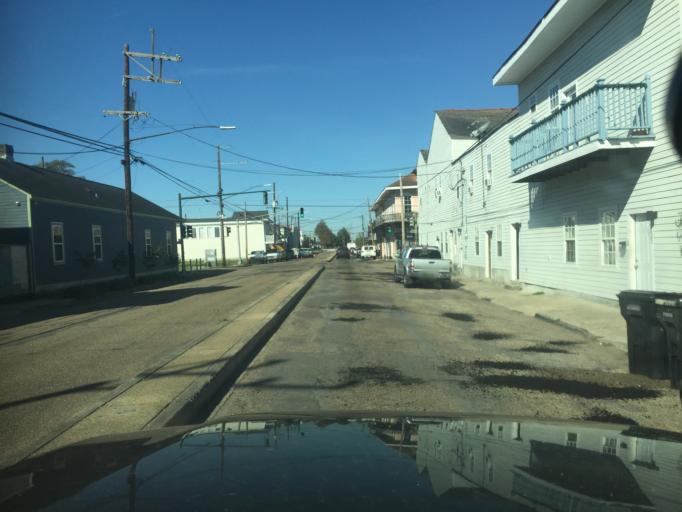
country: US
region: Louisiana
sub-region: Orleans Parish
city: New Orleans
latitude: 29.9402
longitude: -90.0774
